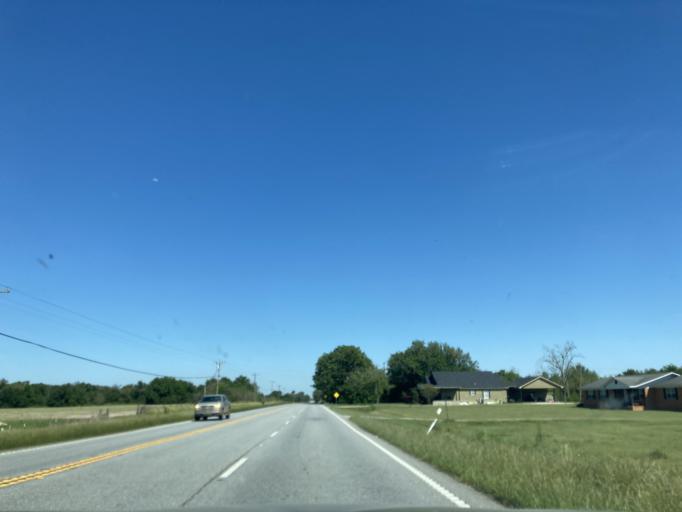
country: US
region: Georgia
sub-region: Miller County
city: Colquitt
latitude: 31.1849
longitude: -84.5912
